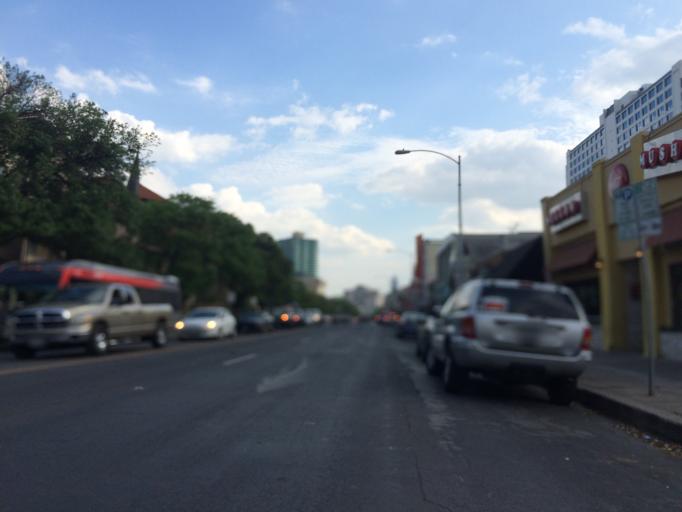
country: US
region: Texas
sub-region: Travis County
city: Austin
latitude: 30.2888
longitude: -97.7416
